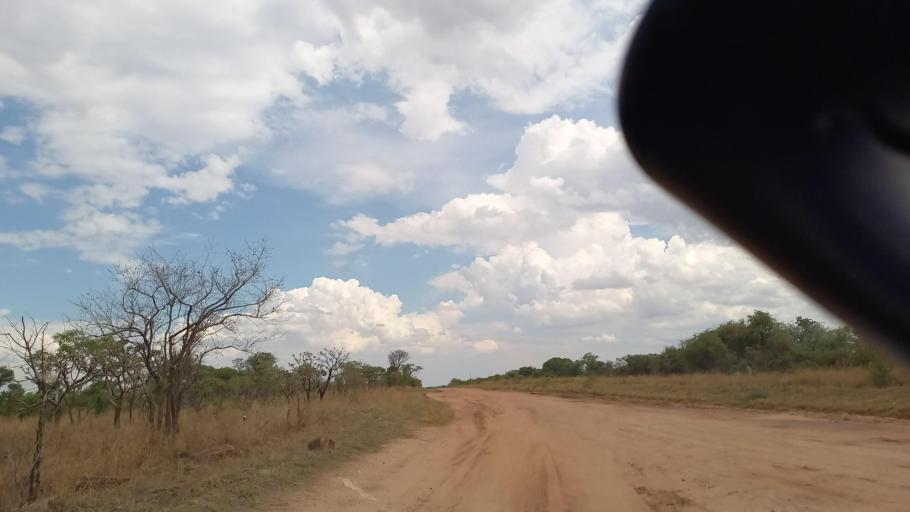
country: ZM
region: Southern
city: Nakambala
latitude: -16.0582
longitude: 27.9897
